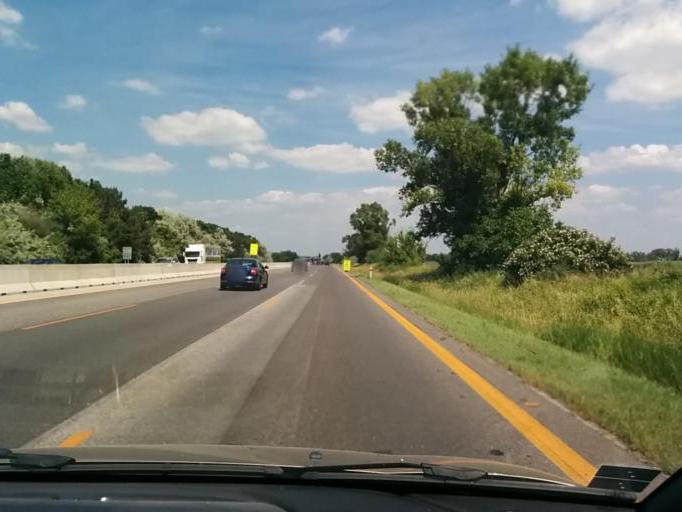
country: SK
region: Trnavsky
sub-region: Okres Trnava
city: Trnava
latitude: 48.3196
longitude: 17.5950
